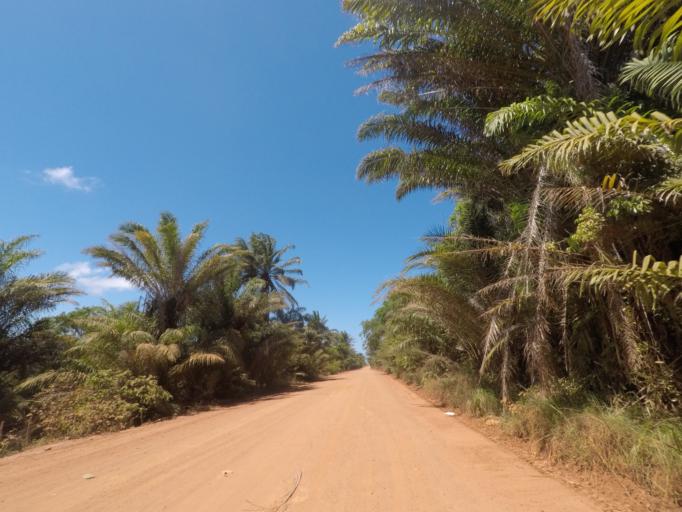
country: BR
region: Bahia
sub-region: Marau
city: Marau
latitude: -13.9625
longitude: -38.9469
